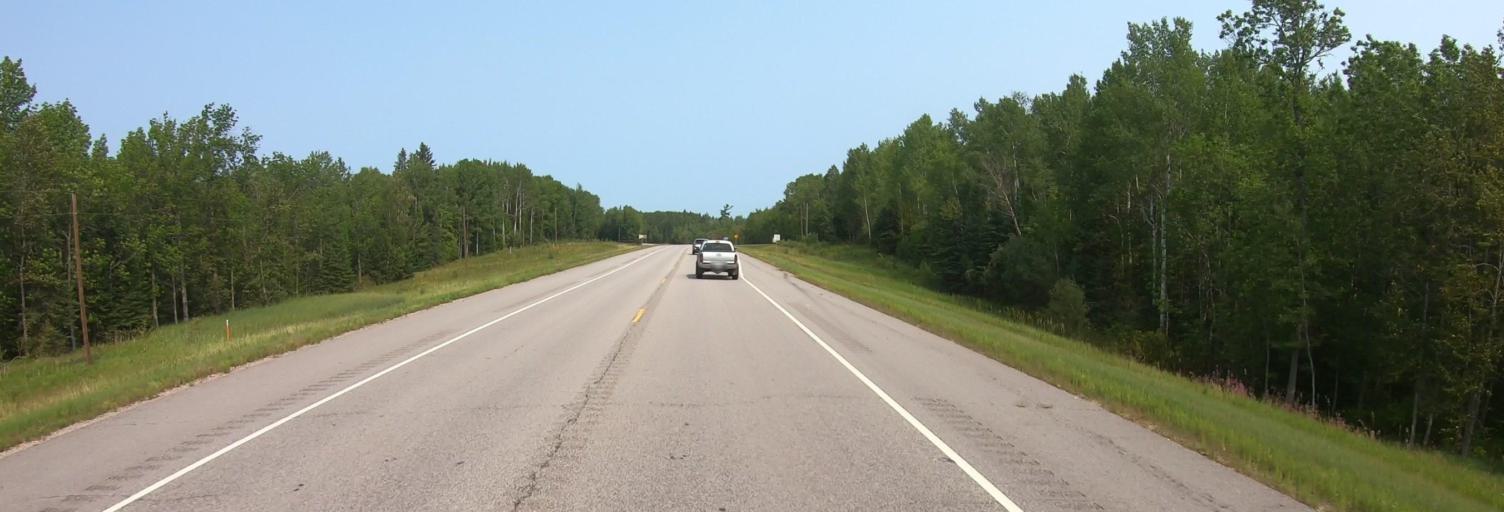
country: CA
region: Ontario
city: Fort Frances
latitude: 48.3598
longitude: -92.9632
